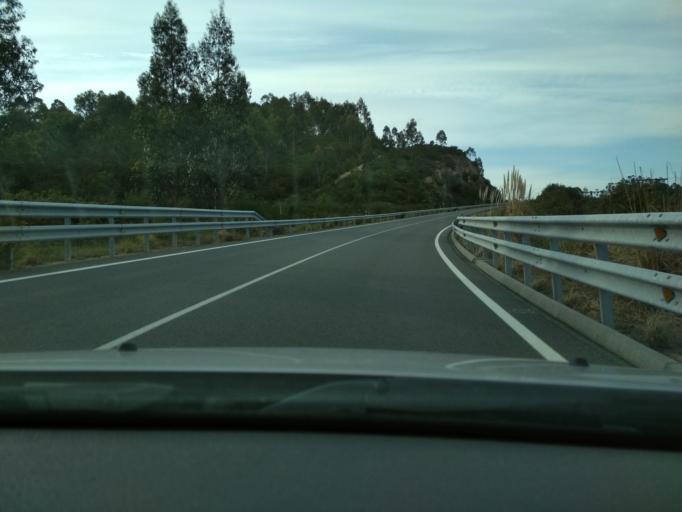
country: ES
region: Galicia
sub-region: Provincia da Coruna
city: Culleredo
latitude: 43.2886
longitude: -8.4017
